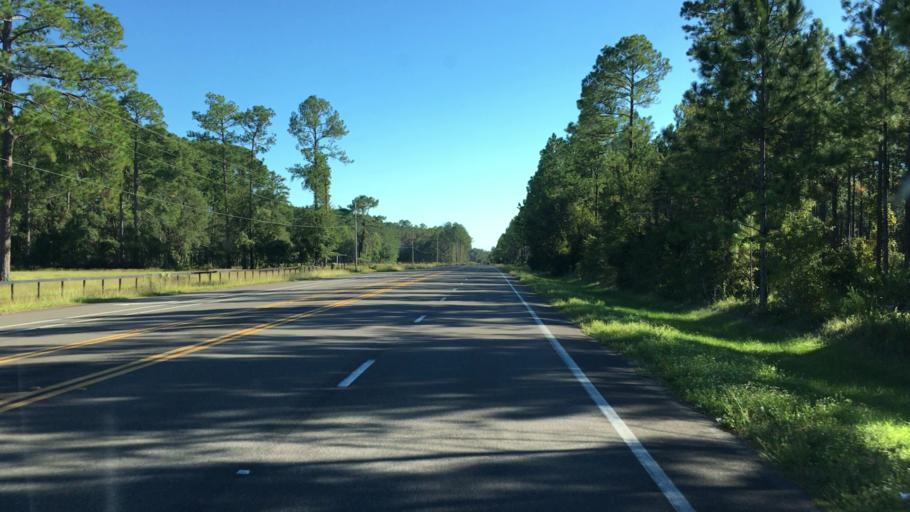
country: US
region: Florida
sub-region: Alachua County
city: Gainesville
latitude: 29.7541
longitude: -82.2782
